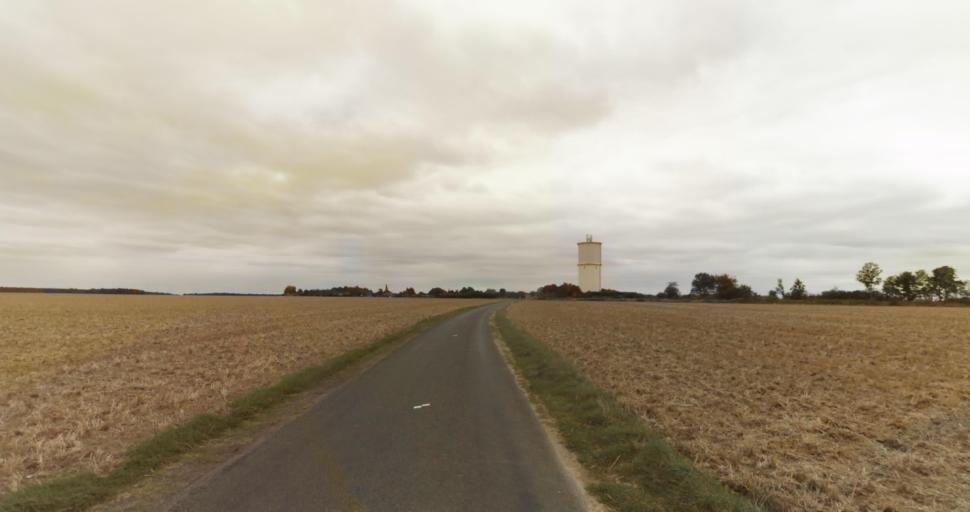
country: FR
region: Haute-Normandie
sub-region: Departement de l'Eure
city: Evreux
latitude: 48.9813
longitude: 1.2352
